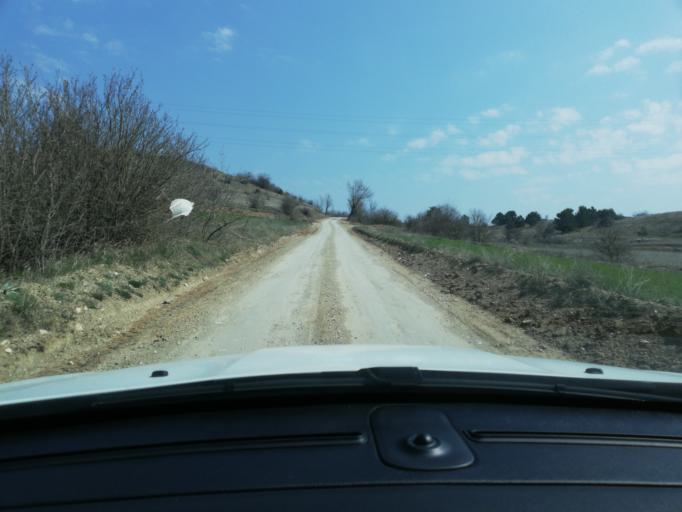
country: TR
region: Kastamonu
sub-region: Cide
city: Kastamonu
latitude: 41.4656
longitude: 33.7717
